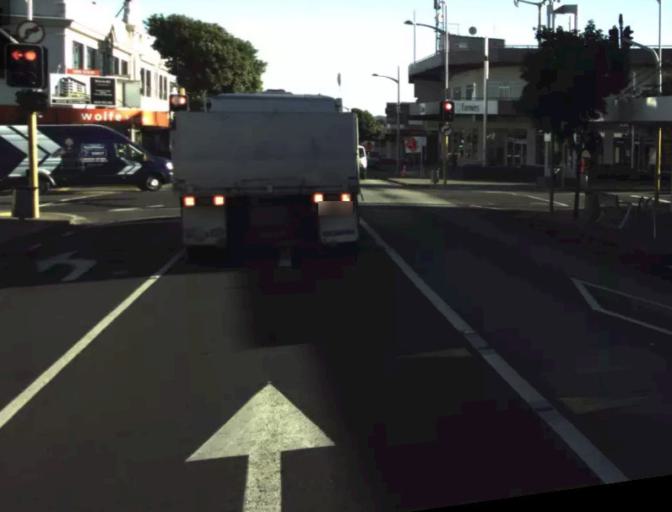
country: NZ
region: Auckland
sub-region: Auckland
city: Papakura
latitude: -37.0626
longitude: 174.9422
